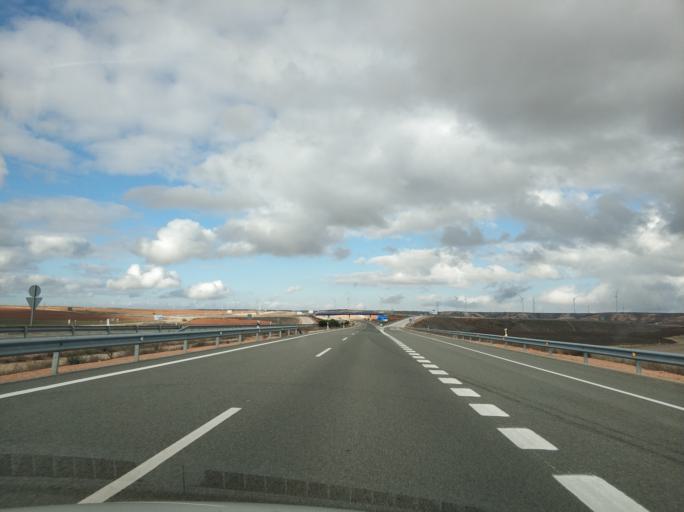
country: ES
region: Castille and Leon
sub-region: Provincia de Soria
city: Alcubilla de las Penas
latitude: 41.2566
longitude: -2.4735
